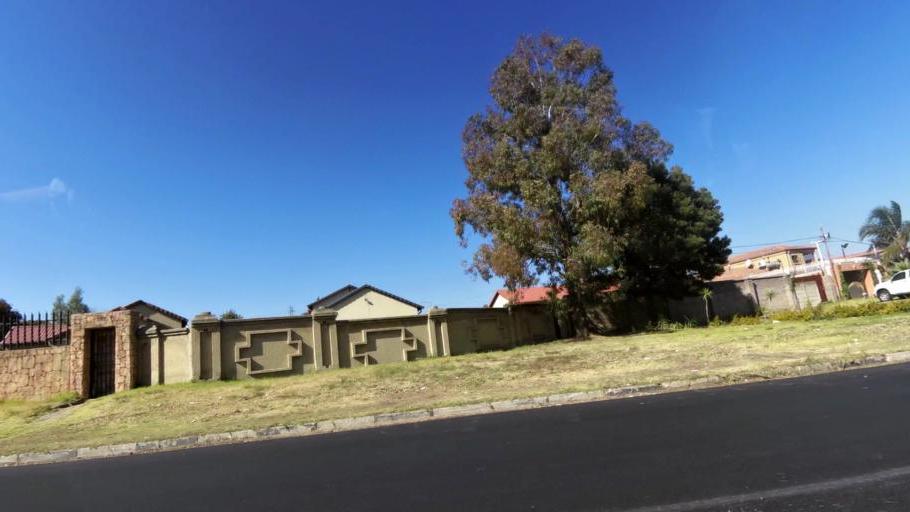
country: ZA
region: Gauteng
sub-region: City of Johannesburg Metropolitan Municipality
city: Johannesburg
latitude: -26.2470
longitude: 27.9990
